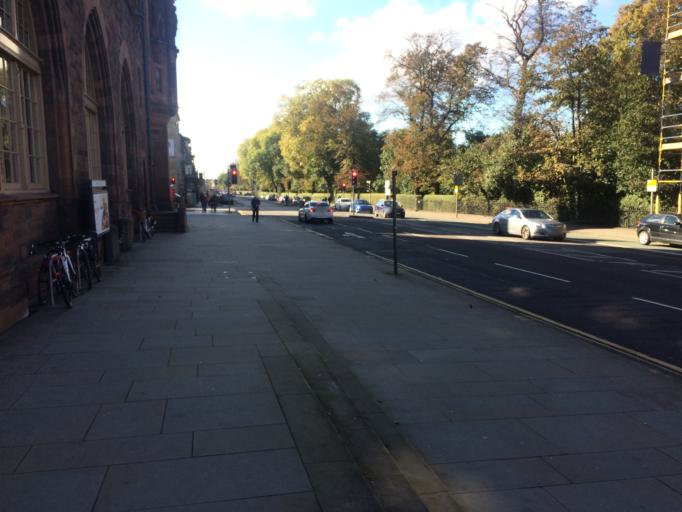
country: GB
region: Scotland
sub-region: Edinburgh
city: Edinburgh
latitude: 55.9559
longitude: -3.1938
